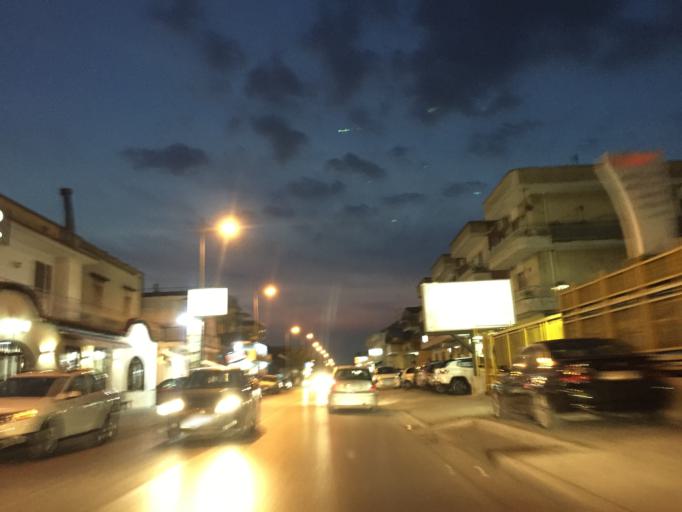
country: IT
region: Campania
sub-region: Provincia di Salerno
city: San Lorenzo
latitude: 40.7481
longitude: 14.5886
